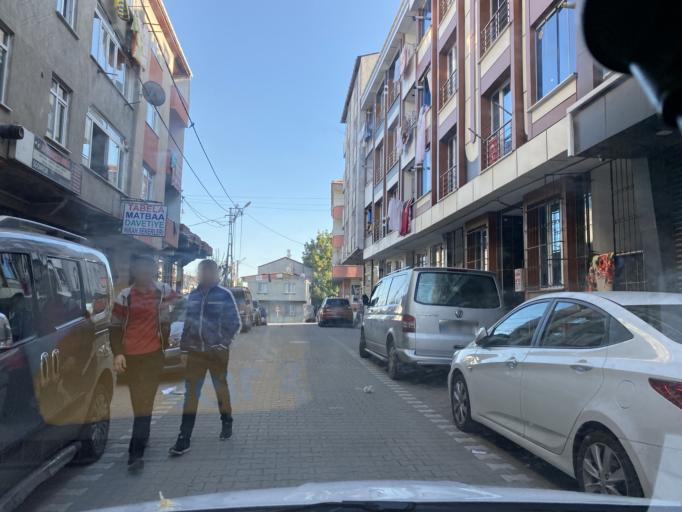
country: TR
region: Istanbul
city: Esenyurt
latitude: 41.0386
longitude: 28.6933
